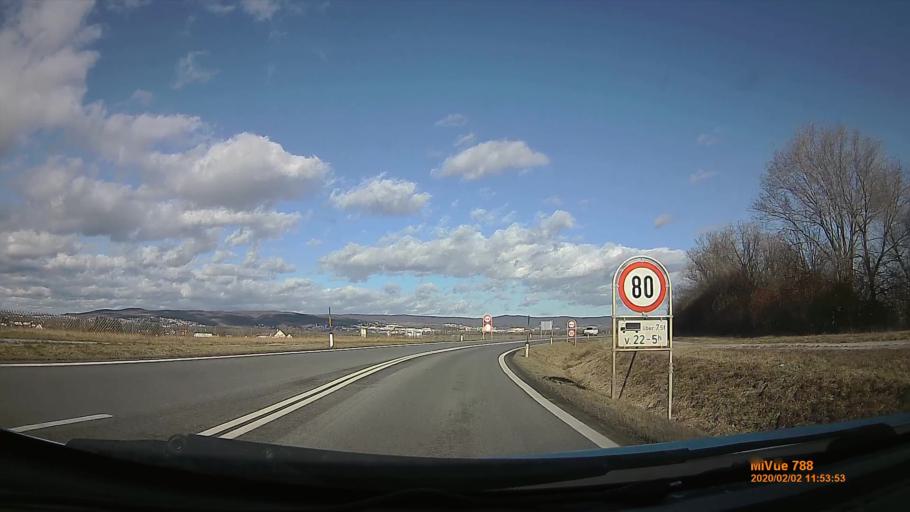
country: AT
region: Burgenland
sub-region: Eisenstadt-Umgebung
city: Wulkaprodersdorf
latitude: 47.7887
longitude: 16.5156
